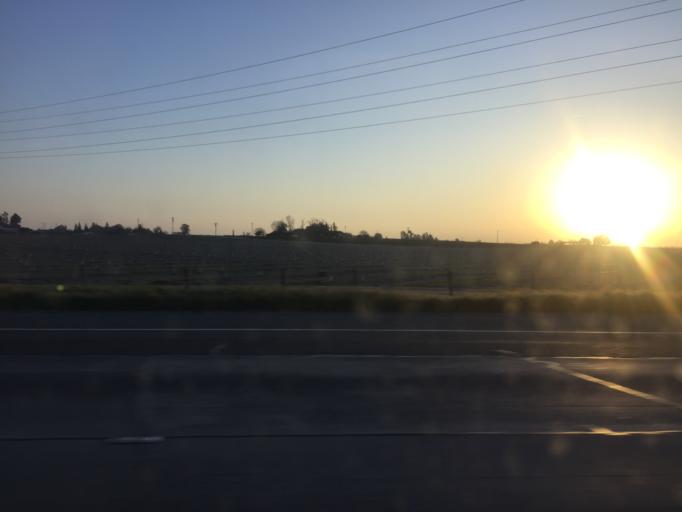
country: US
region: California
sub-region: Fresno County
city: Selma
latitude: 36.5443
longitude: -119.5932
